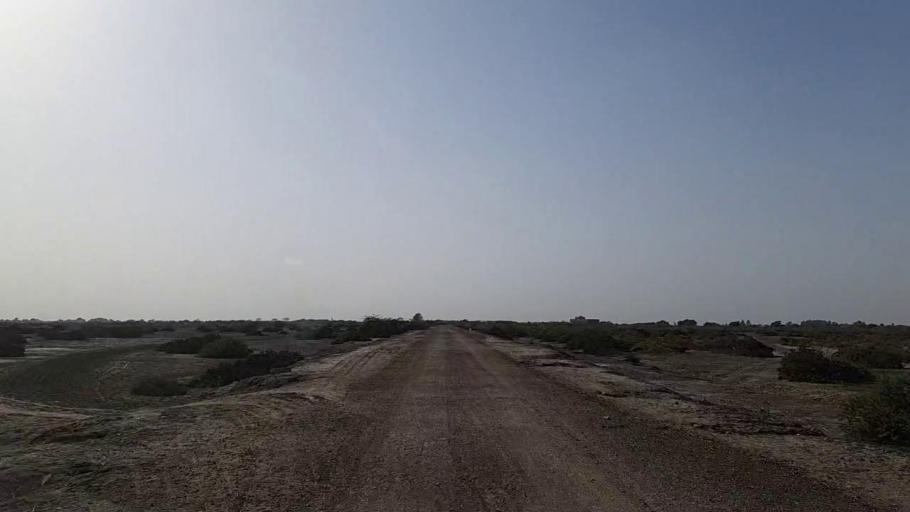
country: PK
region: Sindh
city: Jati
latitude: 24.2855
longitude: 68.2203
